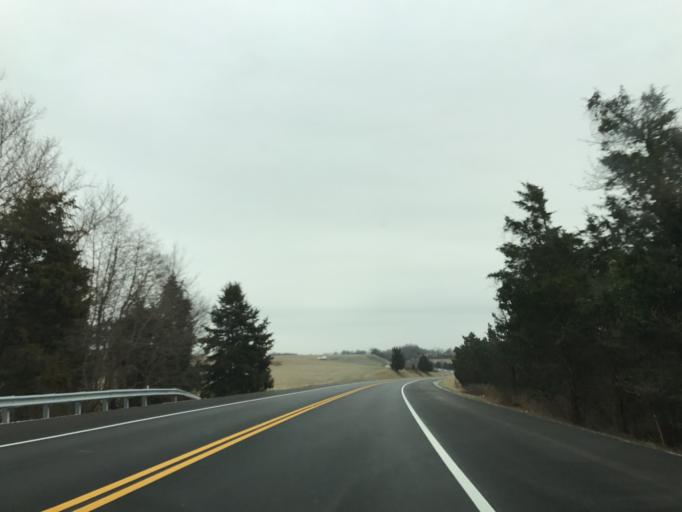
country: US
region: Maryland
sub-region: Carroll County
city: New Windsor
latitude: 39.6173
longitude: -77.0845
